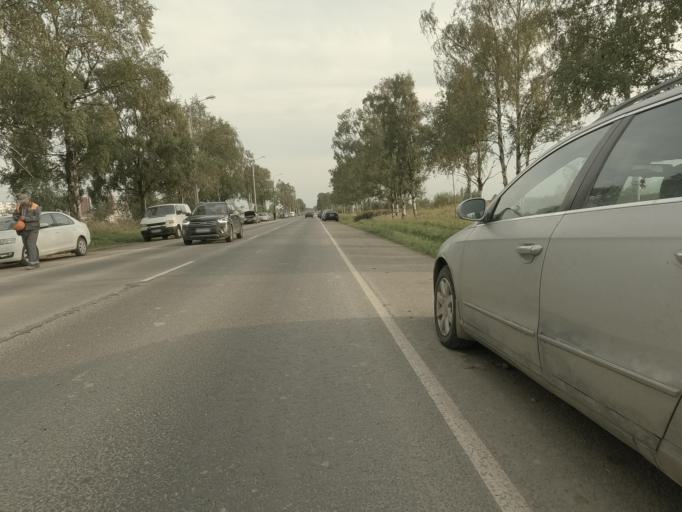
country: RU
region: St.-Petersburg
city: Strel'na
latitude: 59.8472
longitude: 30.0908
